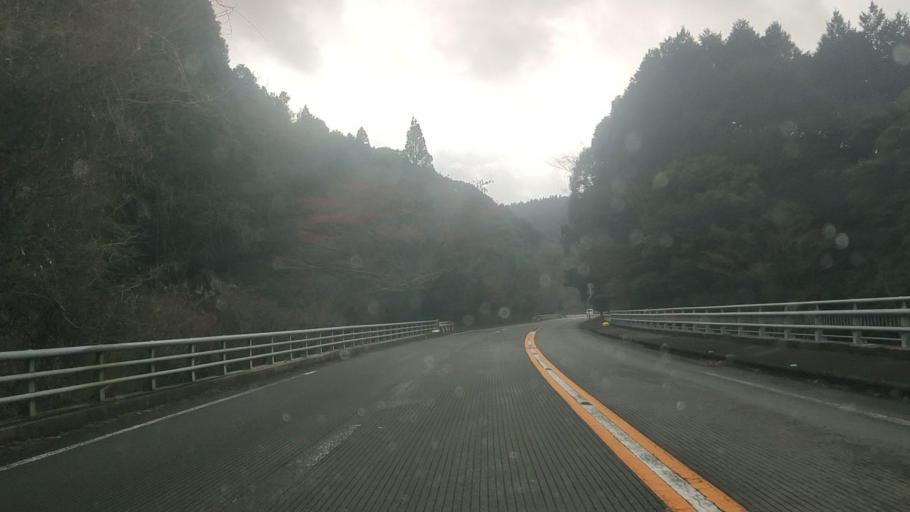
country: JP
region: Kumamoto
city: Hitoyoshi
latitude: 32.1174
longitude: 130.8089
